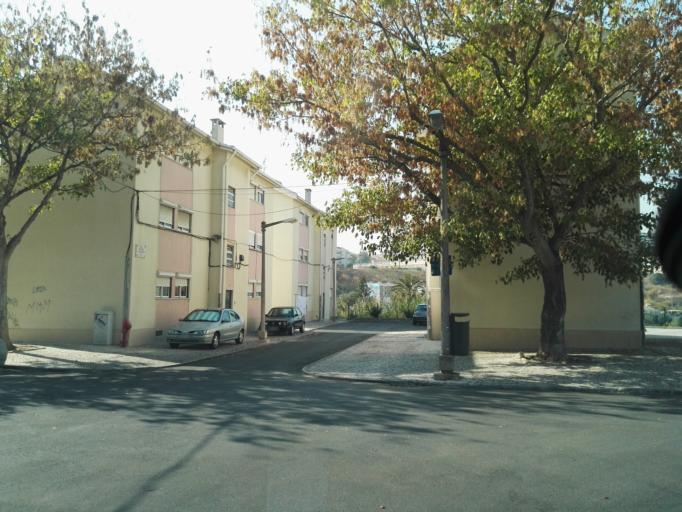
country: PT
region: Lisbon
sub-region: Lisbon
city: Lisbon
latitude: 38.7343
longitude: -9.1156
